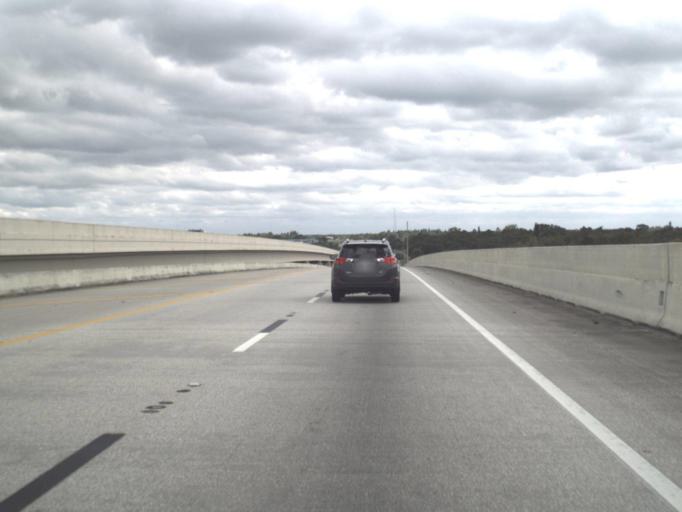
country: US
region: Florida
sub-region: Martin County
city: Palm City
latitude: 27.1169
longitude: -80.2745
